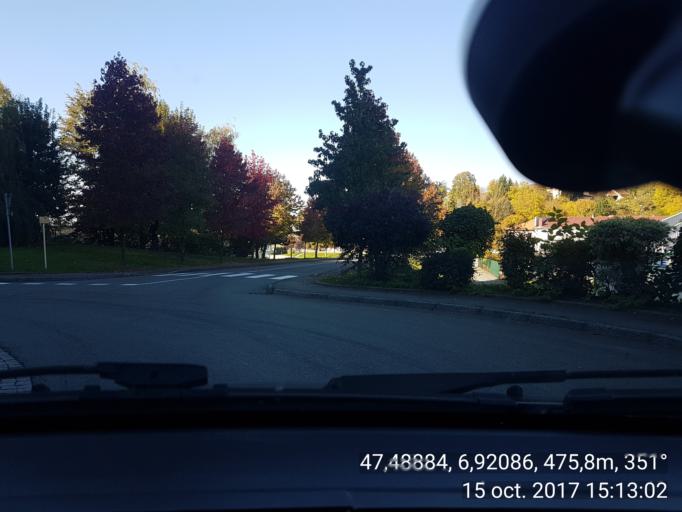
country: FR
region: Franche-Comte
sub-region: Territoire de Belfort
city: Beaucourt
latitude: 47.4889
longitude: 6.9208
